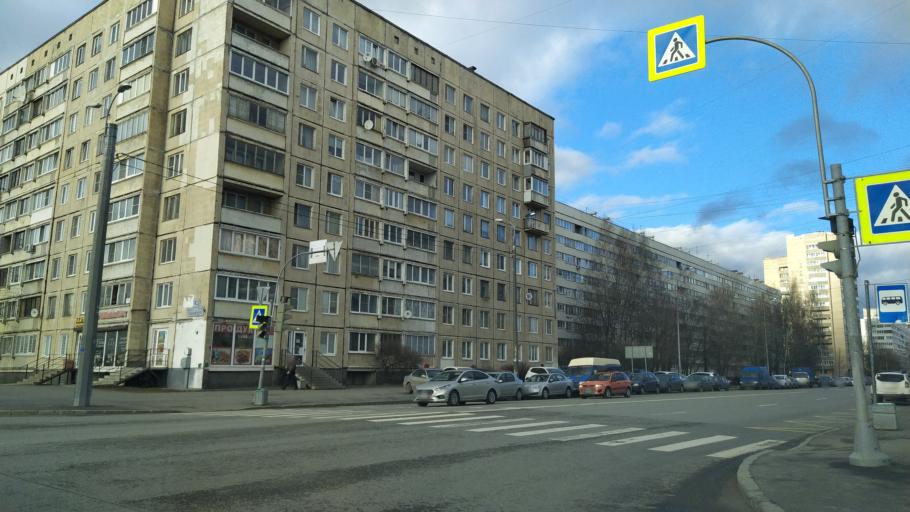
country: RU
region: Leningrad
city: Akademicheskoe
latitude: 60.0335
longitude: 30.3795
